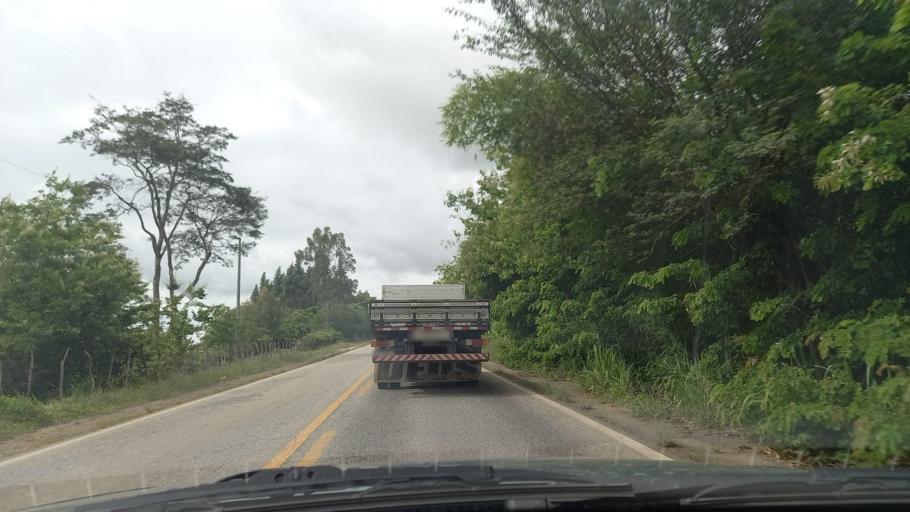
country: BR
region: Pernambuco
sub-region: Canhotinho
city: Canhotinho
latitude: -8.8627
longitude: -36.1820
